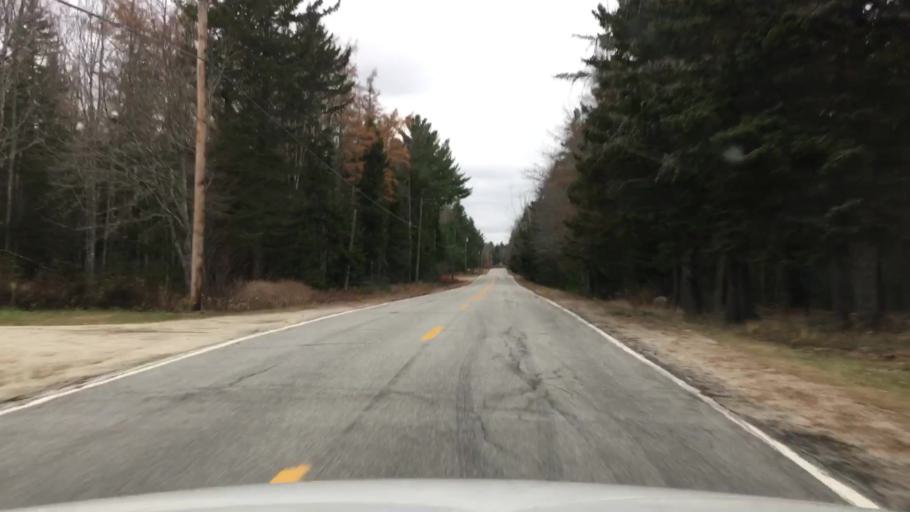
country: US
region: Maine
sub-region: Hancock County
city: Sedgwick
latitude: 44.2828
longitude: -68.5543
